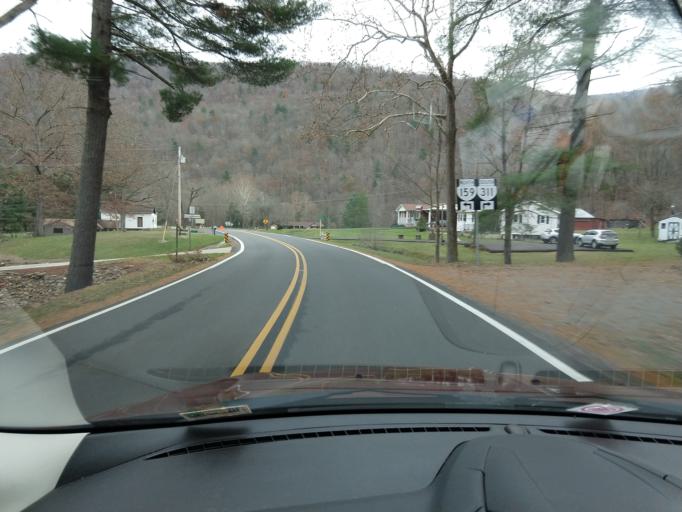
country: US
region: West Virginia
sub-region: Greenbrier County
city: White Sulphur Springs
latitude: 37.7197
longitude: -80.2041
